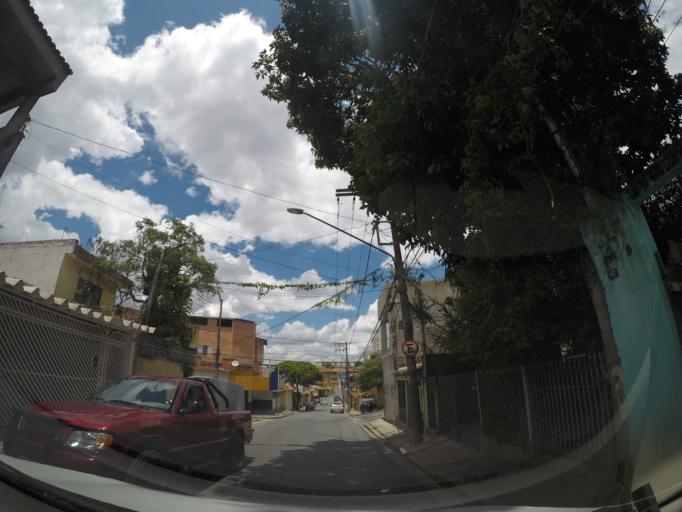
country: BR
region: Sao Paulo
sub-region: Guarulhos
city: Guarulhos
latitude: -23.4583
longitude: -46.5439
